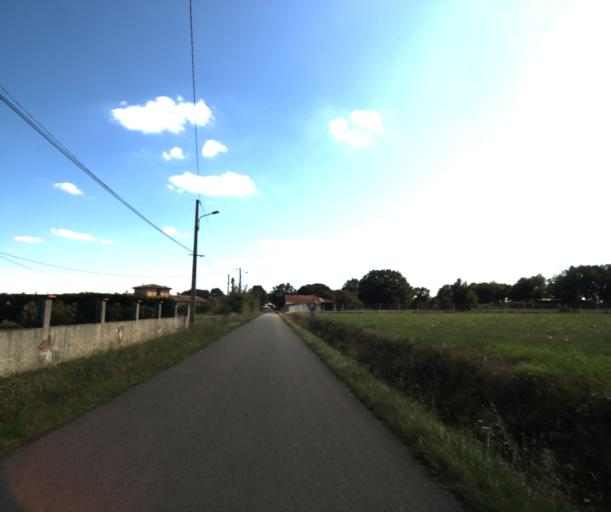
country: FR
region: Midi-Pyrenees
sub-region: Departement de la Haute-Garonne
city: Saint-Lys
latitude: 43.5051
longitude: 1.2077
